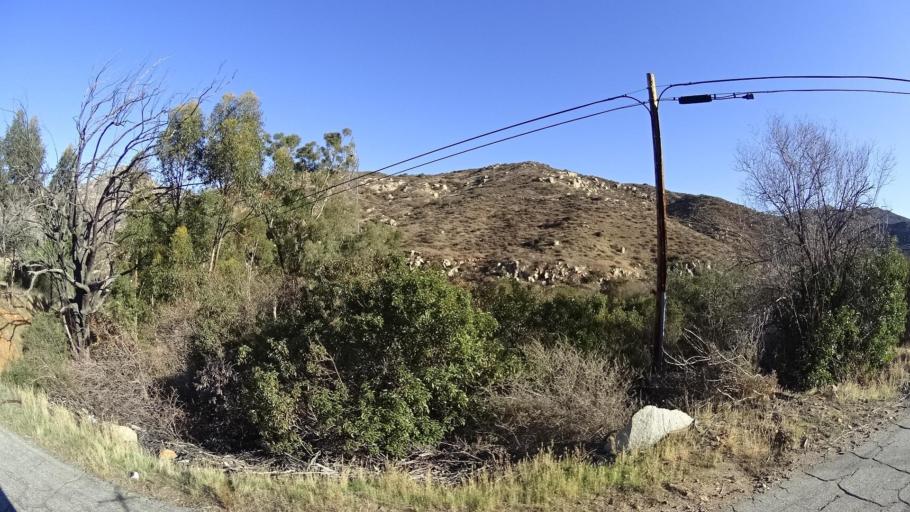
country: MX
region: Baja California
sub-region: Tecate
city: Lomas de Santa Anita
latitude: 32.6043
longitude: -116.6872
